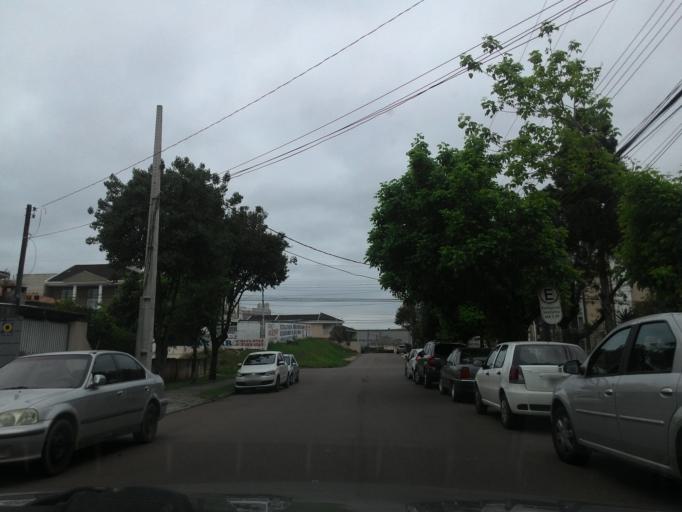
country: BR
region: Parana
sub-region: Curitiba
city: Curitiba
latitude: -25.4810
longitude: -49.2882
